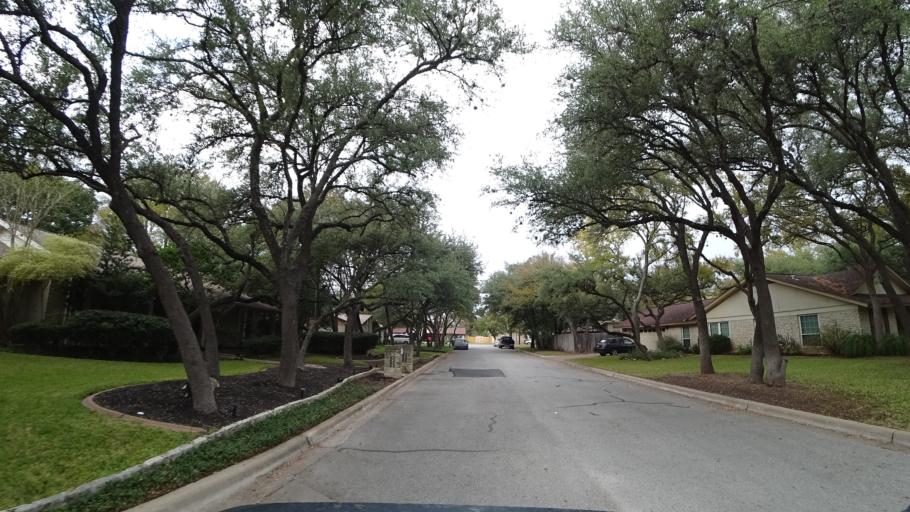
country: US
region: Texas
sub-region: Williamson County
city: Round Rock
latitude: 30.5049
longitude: -97.6968
